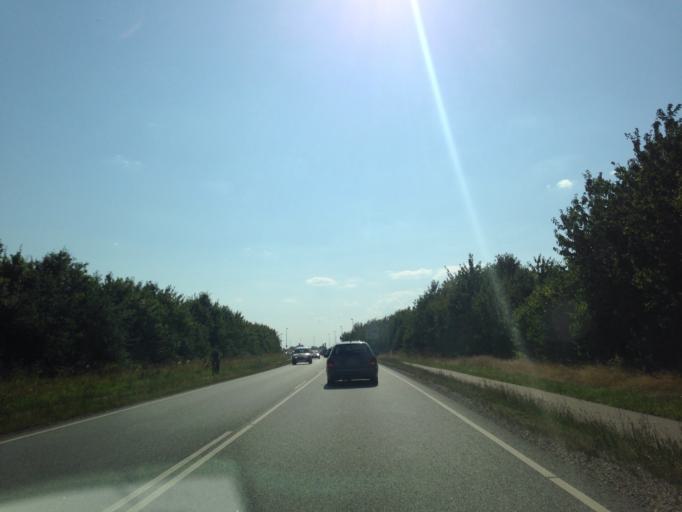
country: DK
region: Zealand
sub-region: Ringsted Kommune
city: Ringsted
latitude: 55.4758
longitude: 11.8323
